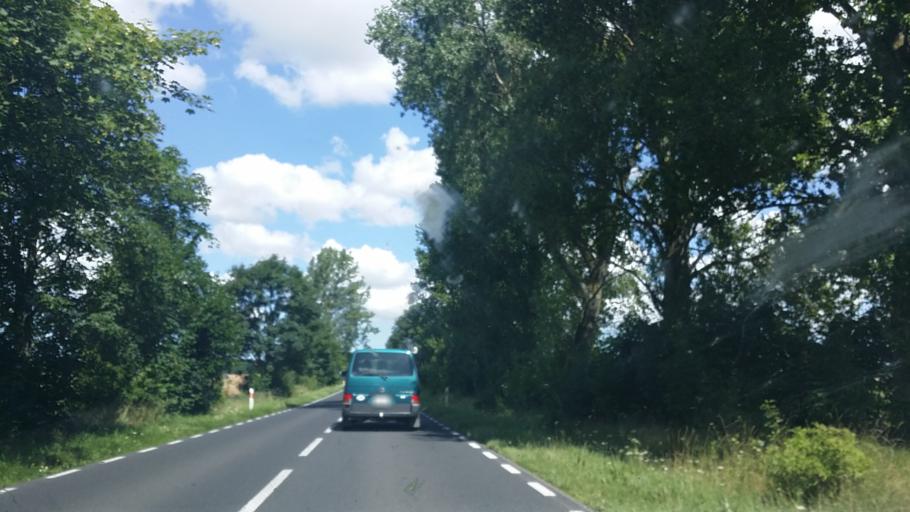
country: PL
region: West Pomeranian Voivodeship
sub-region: Powiat kolobrzeski
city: Goscino
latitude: 53.9865
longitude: 15.6744
